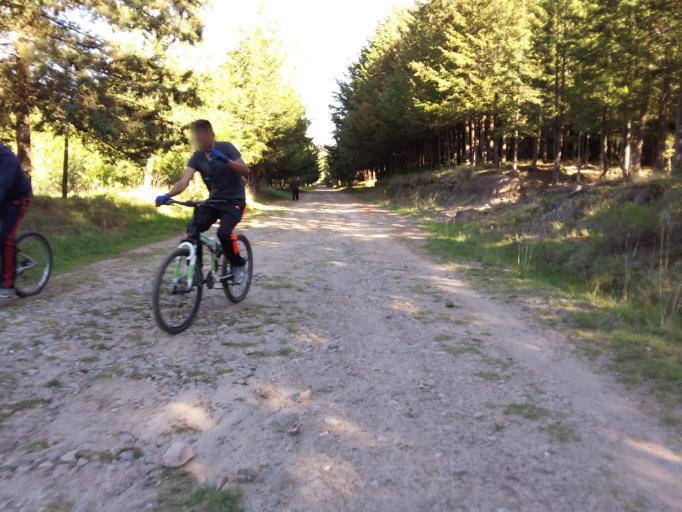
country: MX
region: Mexico
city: San Marcos Yachihuacaltepec
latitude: 19.3124
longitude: -99.6937
